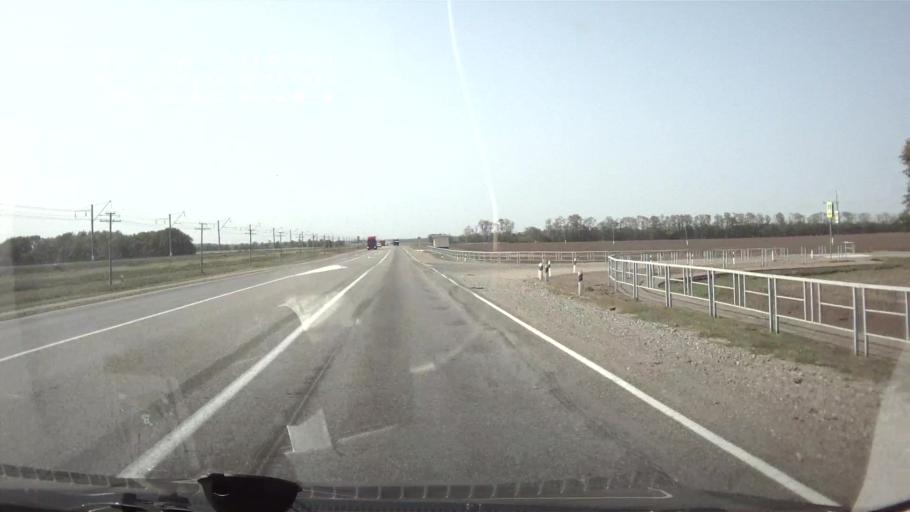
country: RU
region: Krasnodarskiy
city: Ladozhskaya
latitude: 45.3476
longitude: 39.9863
